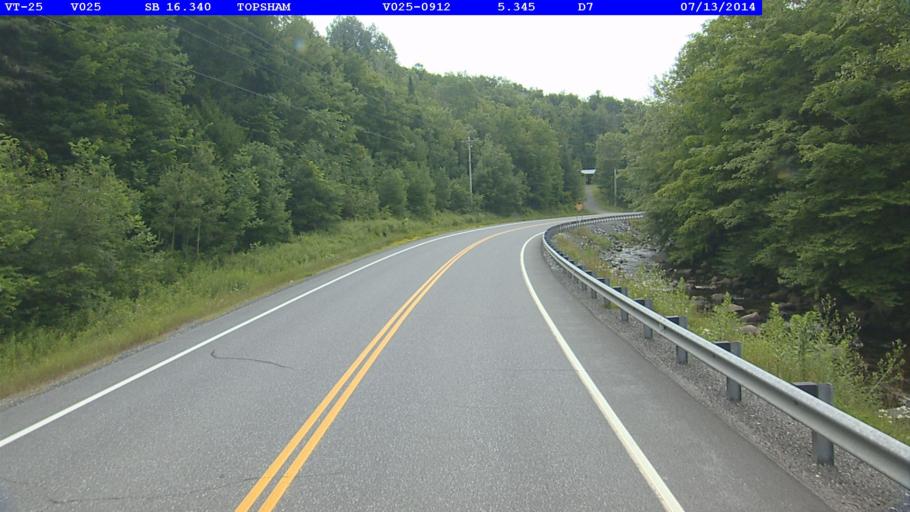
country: US
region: Vermont
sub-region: Orange County
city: Chelsea
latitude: 44.1236
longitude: -72.3063
